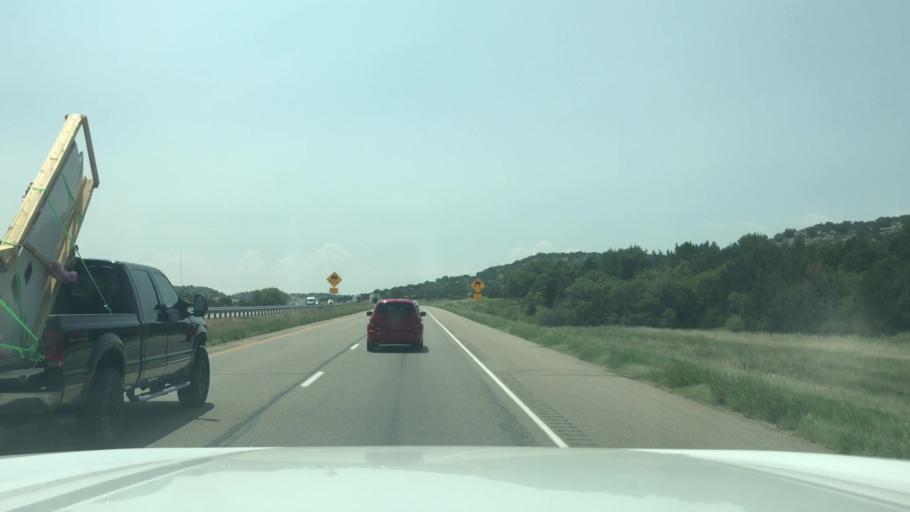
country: US
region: Colorado
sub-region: Pueblo County
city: Colorado City
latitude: 37.9848
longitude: -104.7733
